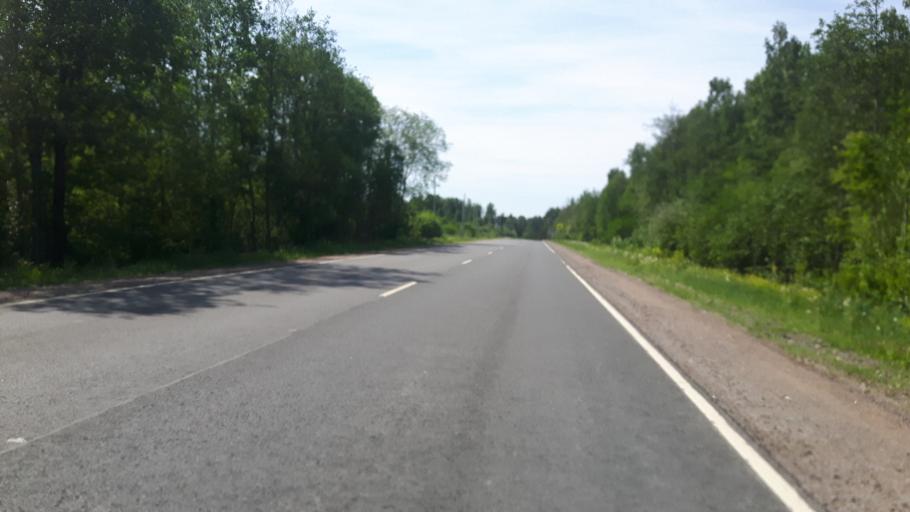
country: RU
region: Leningrad
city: Vistino
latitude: 59.6757
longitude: 28.4517
